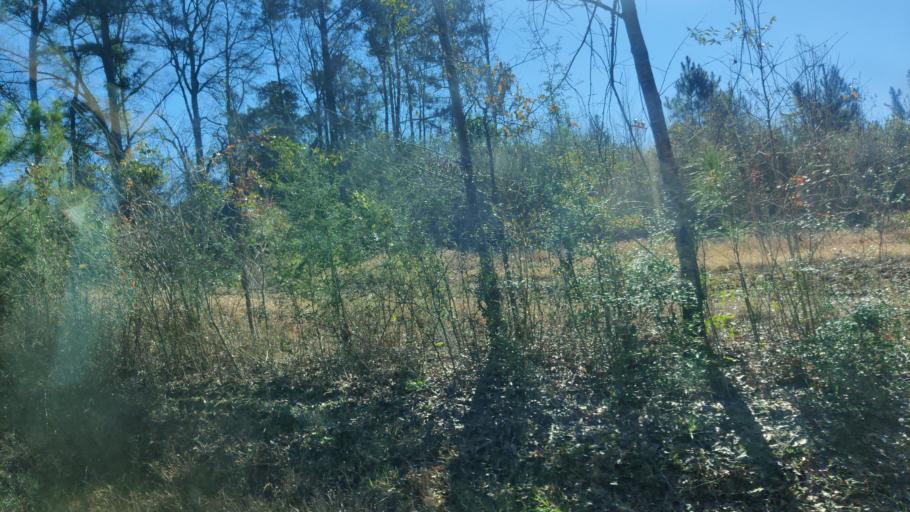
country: US
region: Mississippi
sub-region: Jones County
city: Ellisville
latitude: 31.5453
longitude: -89.3293
